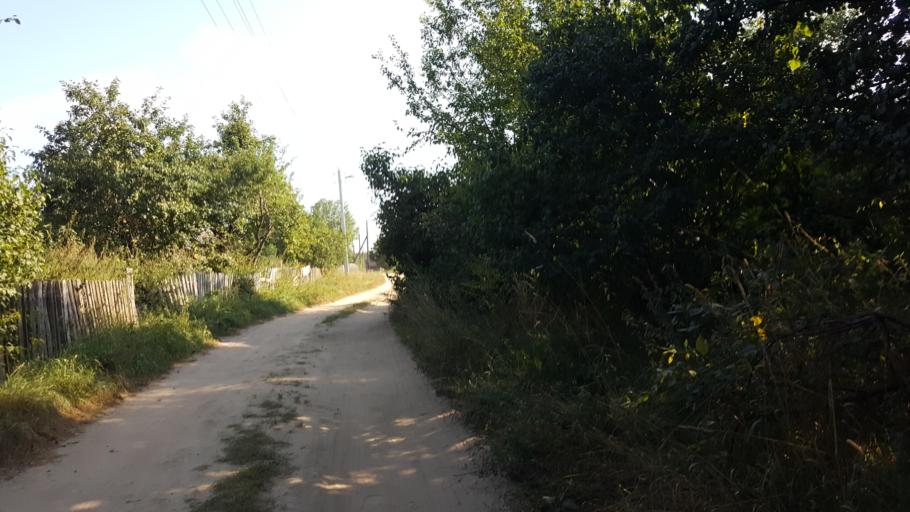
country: PL
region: Podlasie
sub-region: Powiat hajnowski
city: Hajnowka
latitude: 52.5721
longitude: 23.6277
